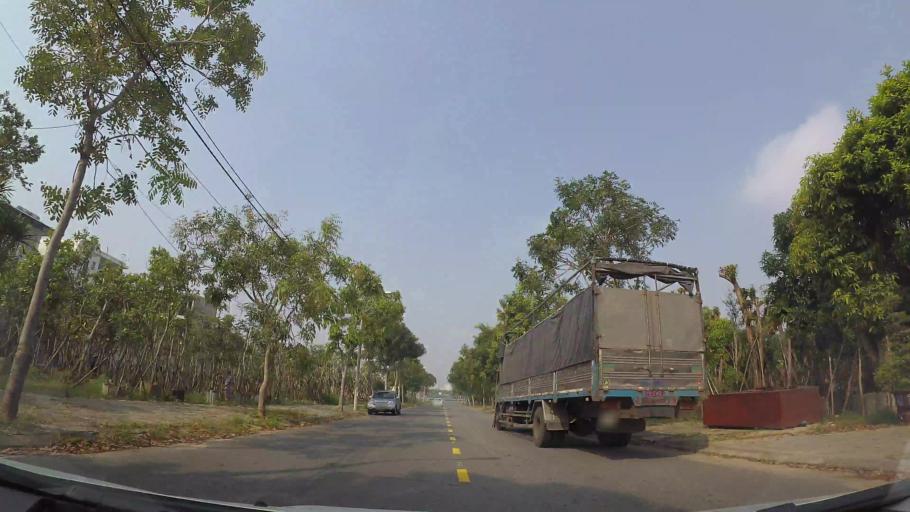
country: VN
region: Da Nang
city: Ngu Hanh Son
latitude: 16.0357
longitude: 108.2397
